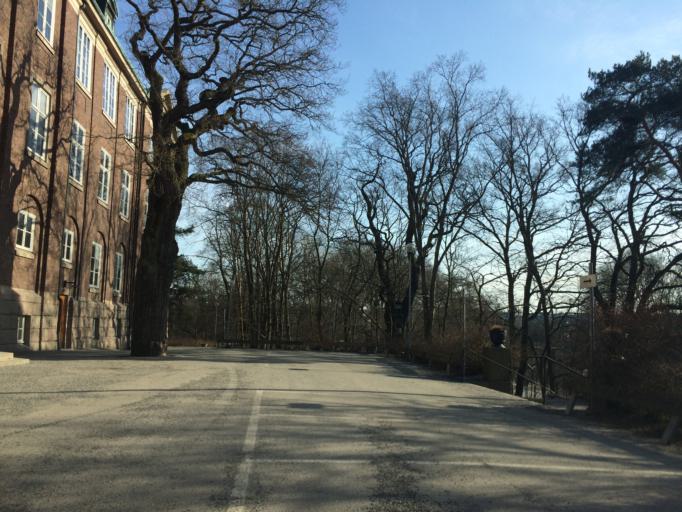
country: SE
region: Stockholm
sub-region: Norrtalje Kommun
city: Bergshamra
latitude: 59.3614
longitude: 18.0541
